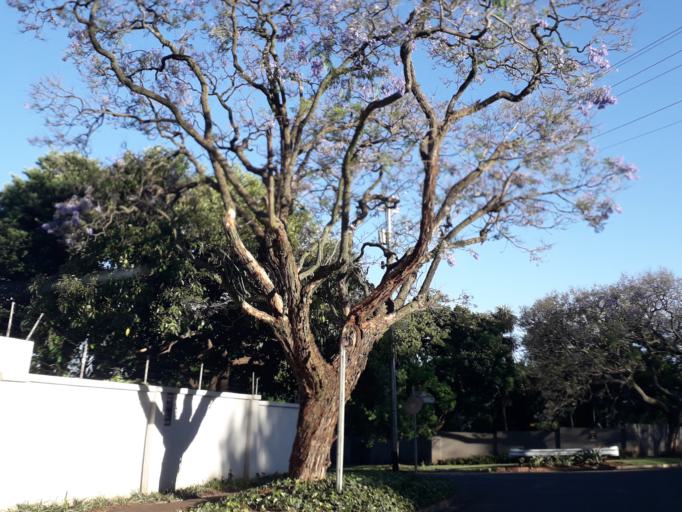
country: ZA
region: Gauteng
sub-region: City of Johannesburg Metropolitan Municipality
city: Johannesburg
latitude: -26.1681
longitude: 28.0108
